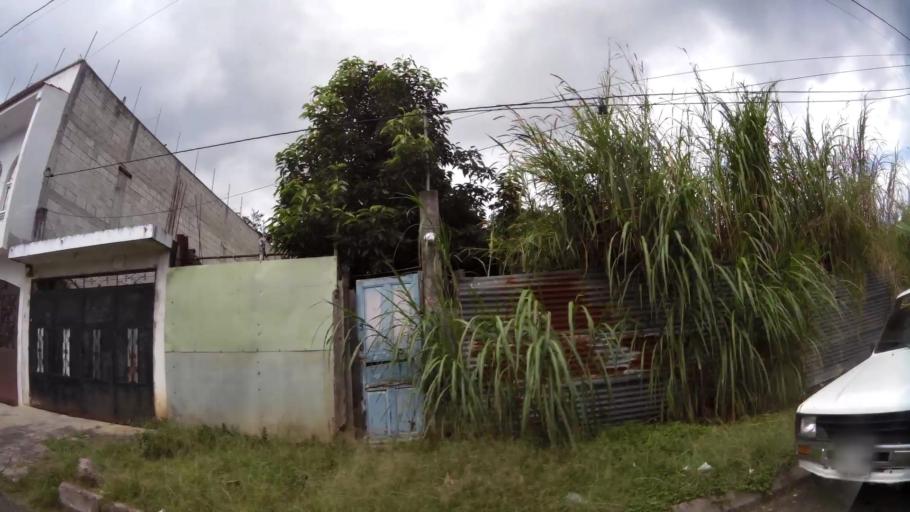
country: GT
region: Guatemala
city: Chinautla
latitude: 14.6852
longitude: -90.5525
